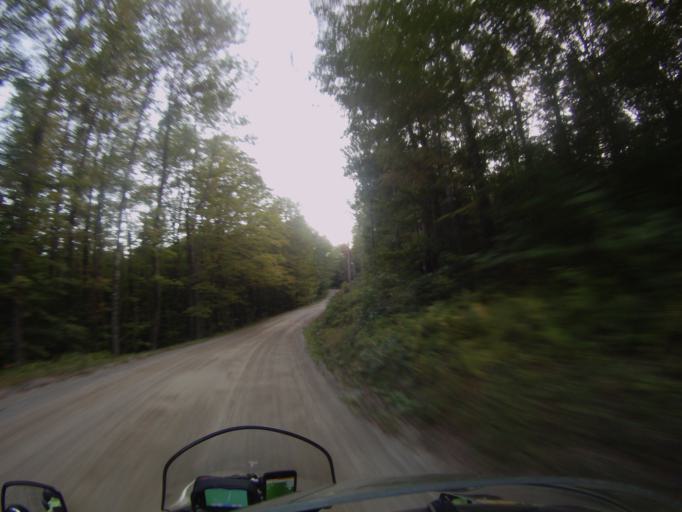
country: US
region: Vermont
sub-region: Addison County
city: Bristol
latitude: 44.0132
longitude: -73.0288
